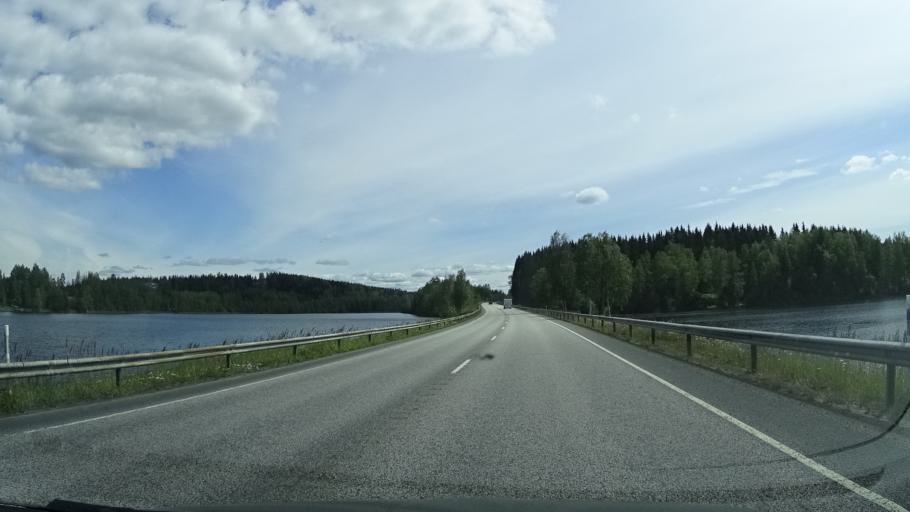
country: FI
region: Central Finland
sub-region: Jyvaeskylae
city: Jyvaeskylae
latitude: 62.2575
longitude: 25.6133
